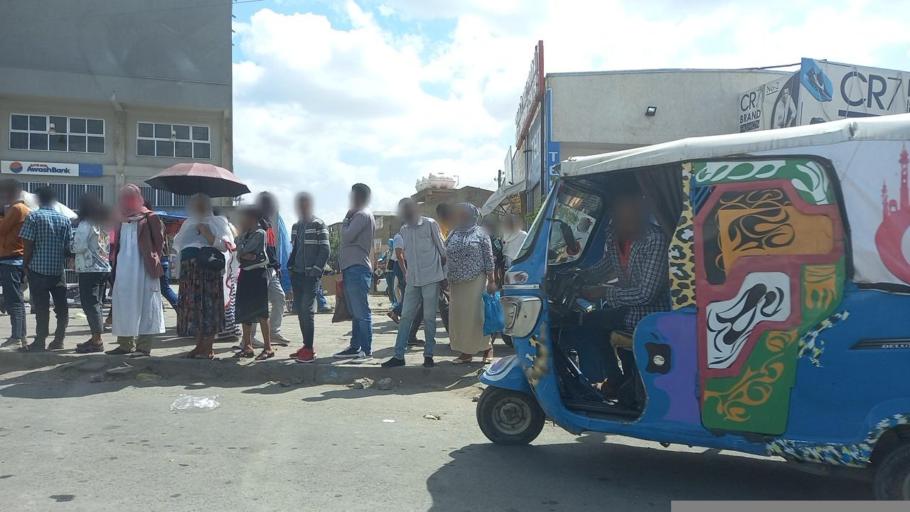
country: ET
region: Adis Abeba
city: Addis Ababa
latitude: 8.9603
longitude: 38.7119
